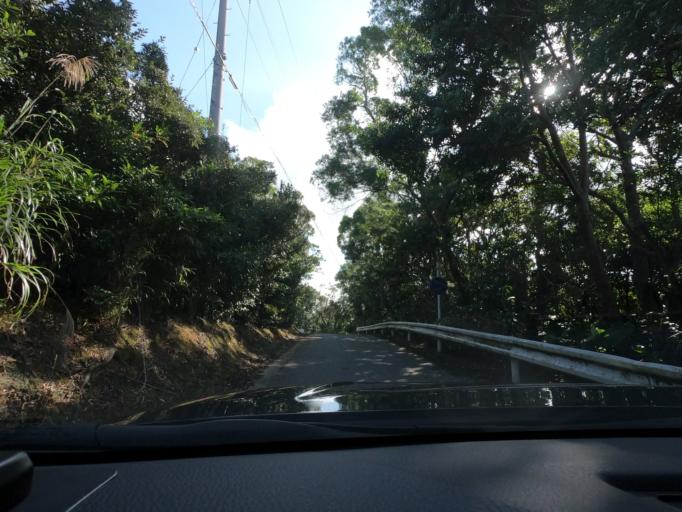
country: JP
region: Okinawa
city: Nago
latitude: 26.7549
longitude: 128.2038
